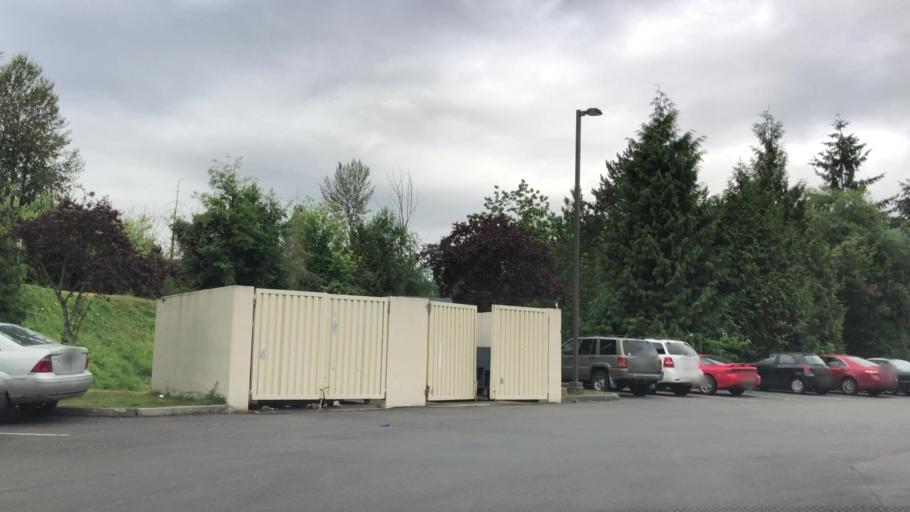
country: US
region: Washington
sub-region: King County
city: Bothell
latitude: 47.7736
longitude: -122.1831
